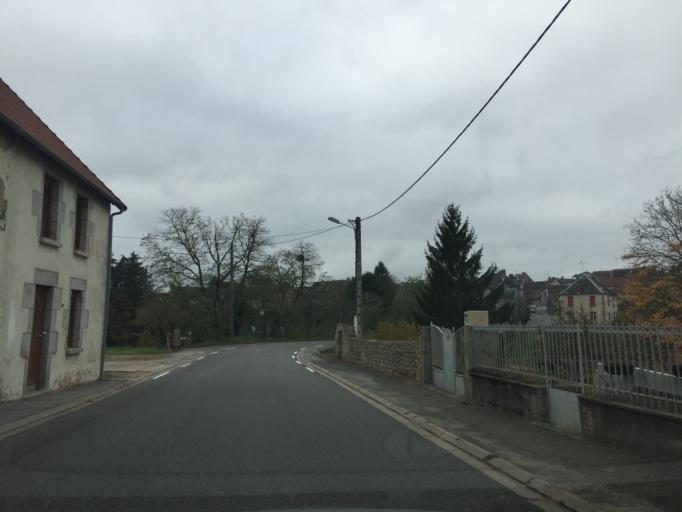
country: FR
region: Limousin
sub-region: Departement de la Creuse
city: Gouzon
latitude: 46.1152
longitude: 2.1773
